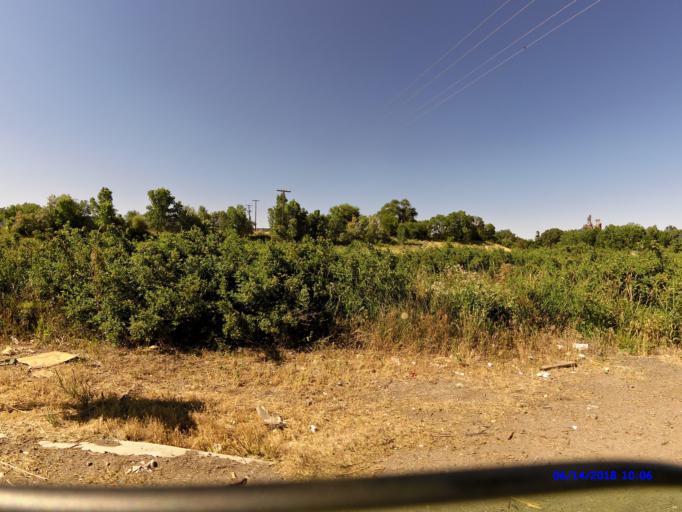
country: US
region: Utah
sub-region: Weber County
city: Ogden
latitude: 41.2265
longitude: -111.9953
